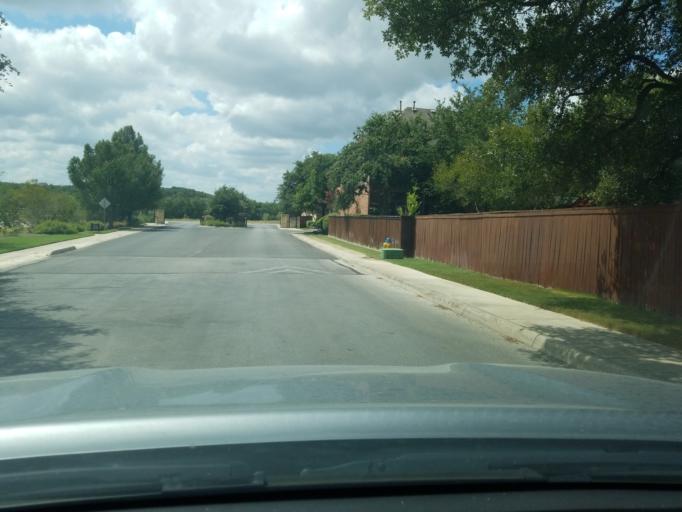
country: US
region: Texas
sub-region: Bexar County
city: Timberwood Park
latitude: 29.6635
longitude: -98.5072
